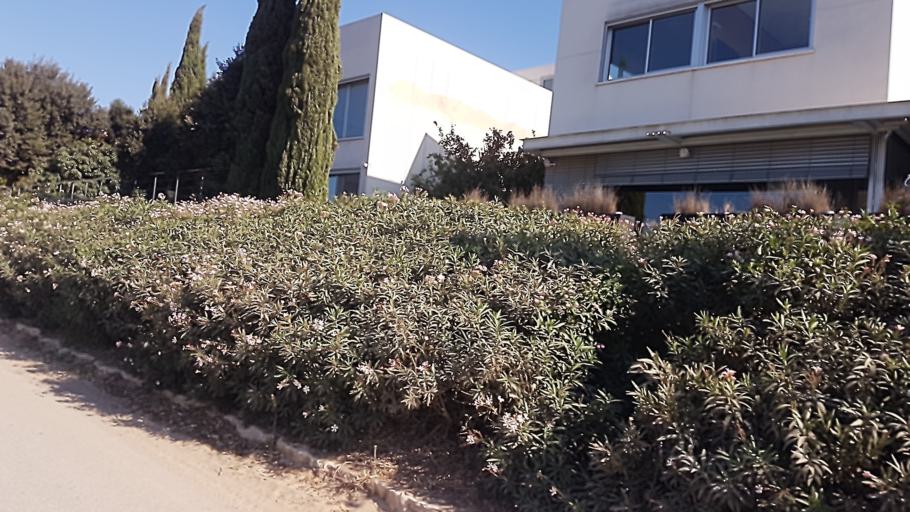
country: IL
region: Central District
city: Ra'anana
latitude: 32.2129
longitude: 34.8919
